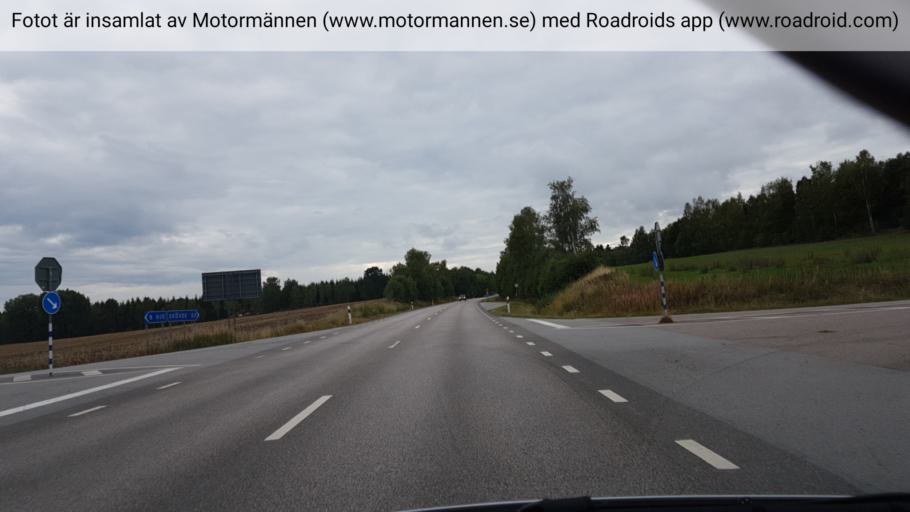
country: SE
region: Vaestra Goetaland
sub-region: Tibro Kommun
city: Tibro
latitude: 58.3414
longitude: 14.1957
